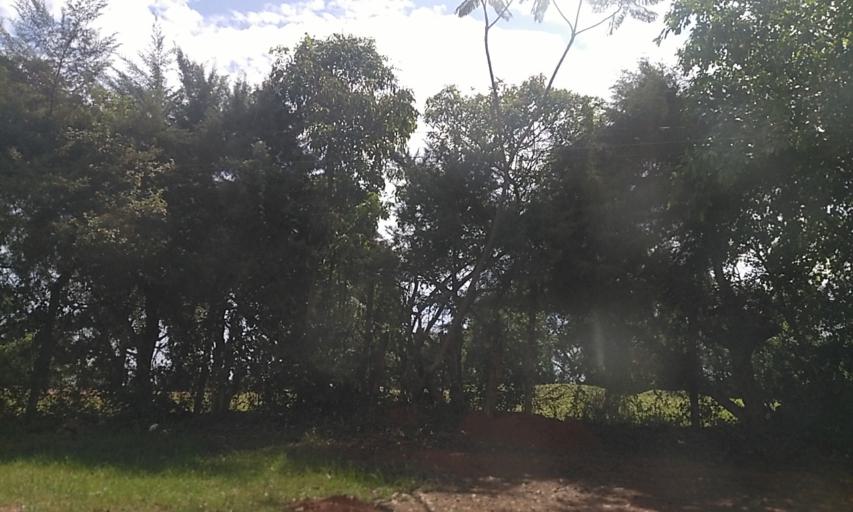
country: UG
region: Central Region
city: Kampala Central Division
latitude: 0.3393
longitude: 32.5901
